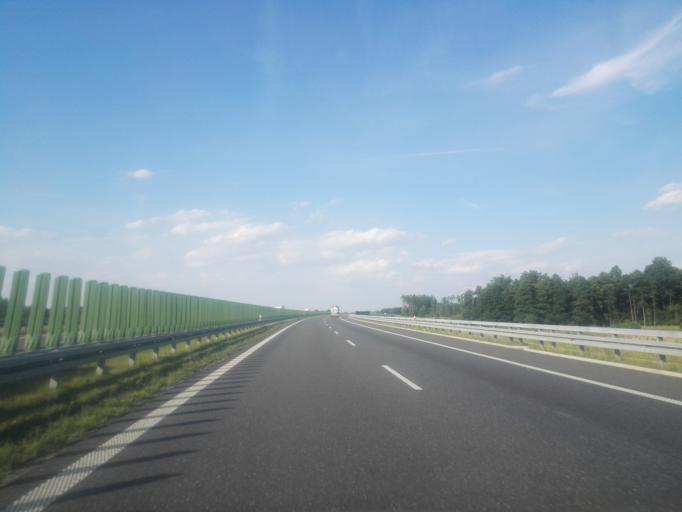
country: PL
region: Lower Silesian Voivodeship
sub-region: Powiat olesnicki
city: Miedzyborz
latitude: 51.2965
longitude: 17.5842
